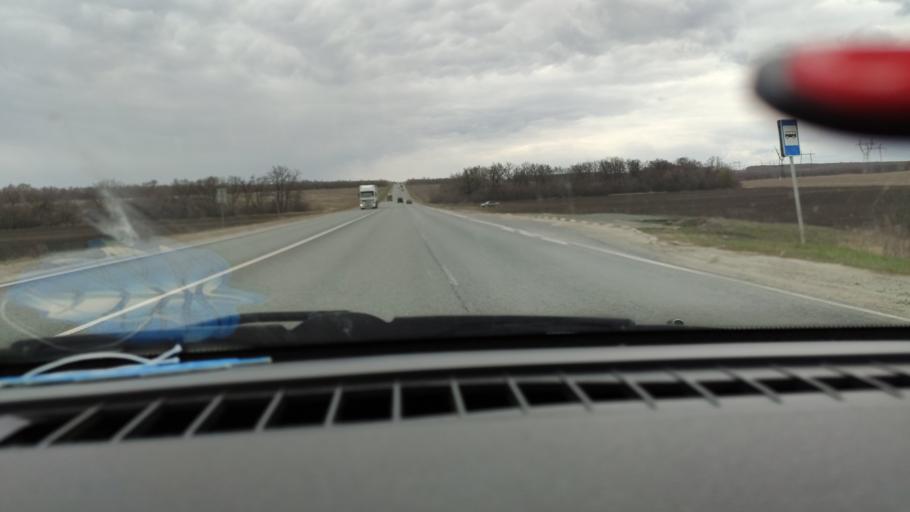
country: RU
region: Saratov
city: Sinodskoye
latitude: 51.9145
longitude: 46.5561
